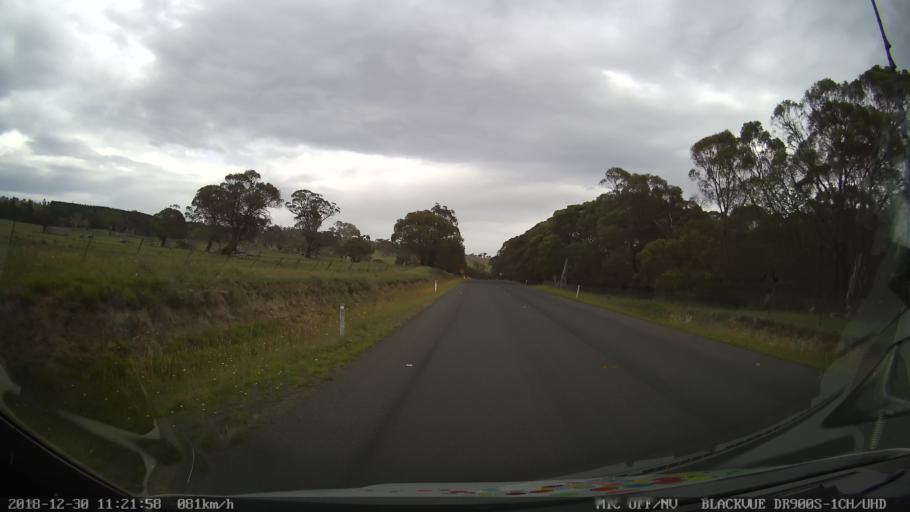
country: AU
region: New South Wales
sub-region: Snowy River
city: Jindabyne
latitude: -36.5055
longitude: 148.6720
